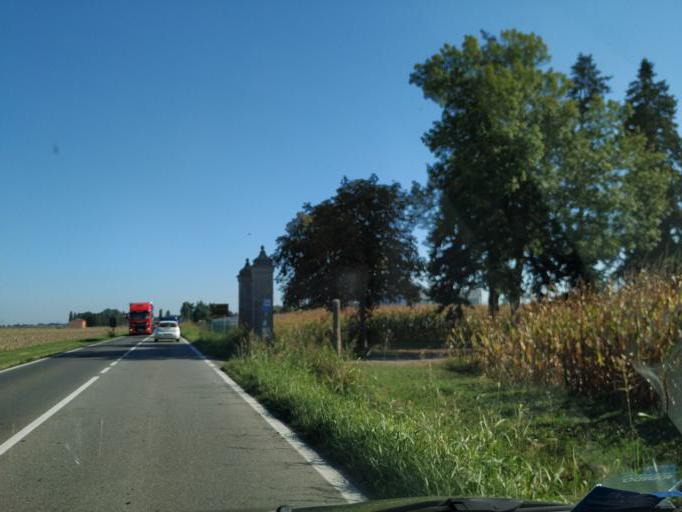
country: IT
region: Emilia-Romagna
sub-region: Provincia di Bologna
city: Decima
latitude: 44.7229
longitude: 11.2569
